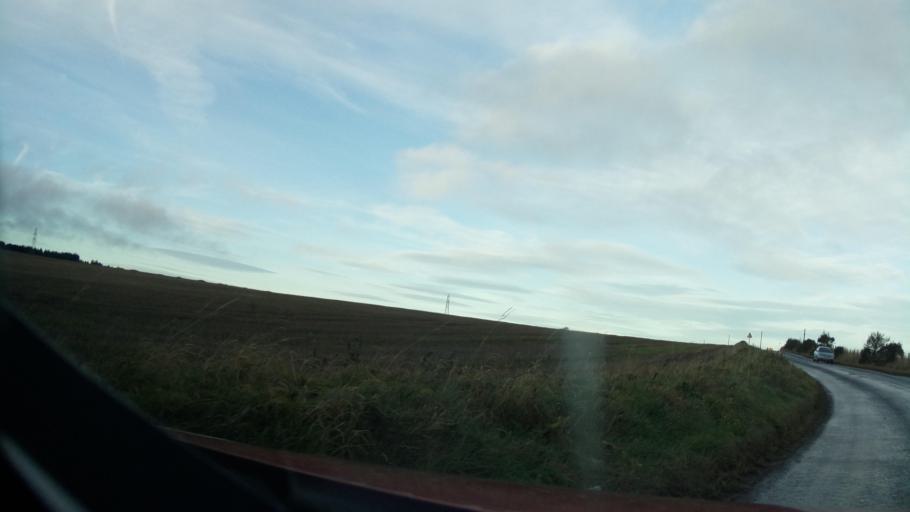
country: GB
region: Scotland
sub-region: Angus
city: Letham
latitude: 56.5419
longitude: -2.7858
